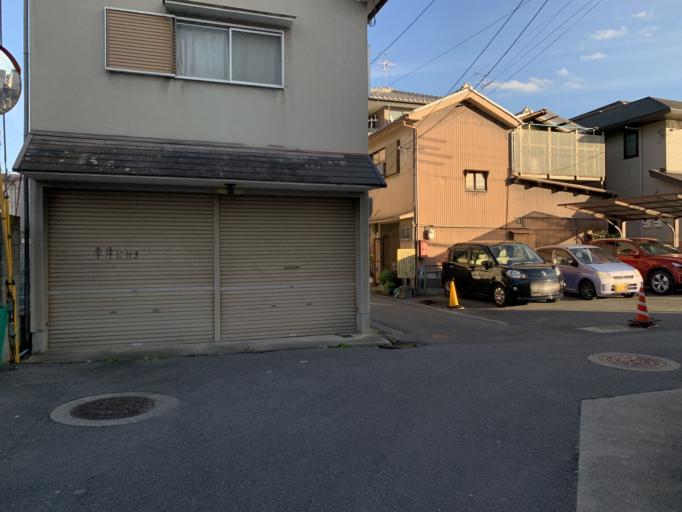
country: JP
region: Nara
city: Nara-shi
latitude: 34.6860
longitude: 135.8268
